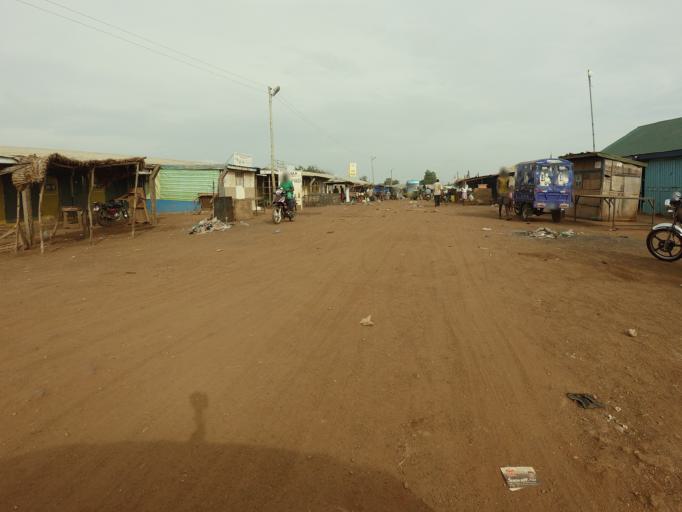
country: GH
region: Northern
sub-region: Yendi
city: Yendi
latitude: 9.9234
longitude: -0.2181
